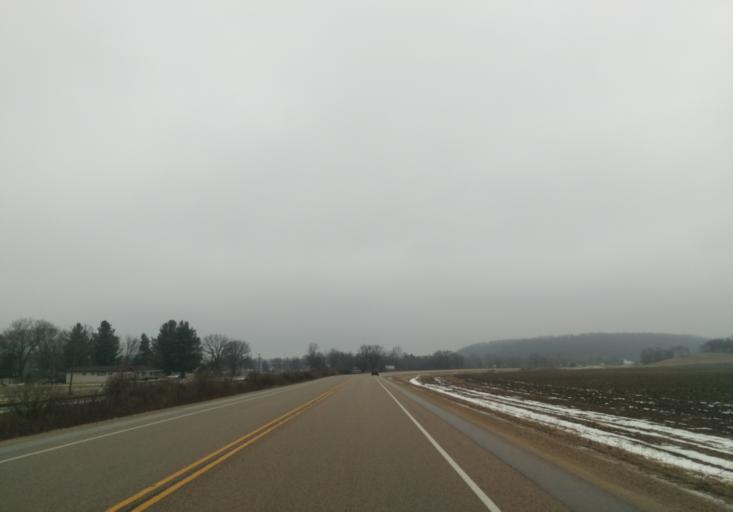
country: US
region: Wisconsin
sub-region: Dane County
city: Black Earth
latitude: 43.1360
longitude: -89.7359
